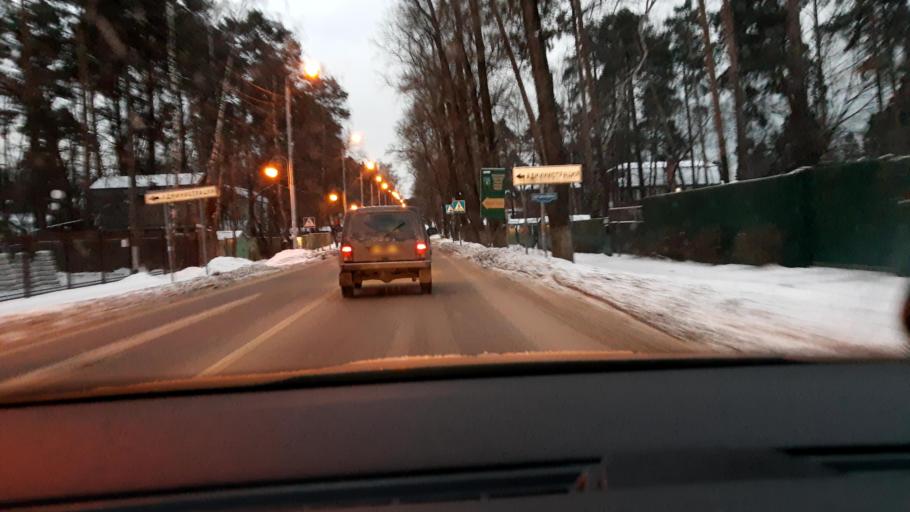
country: RU
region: Moskovskaya
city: Tomilino
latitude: 55.6540
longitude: 37.9525
